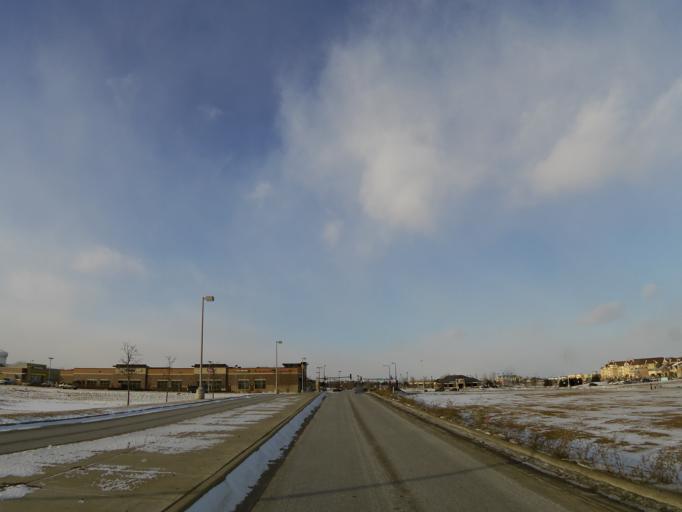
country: US
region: Minnesota
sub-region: Washington County
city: Woodbury
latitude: 44.9394
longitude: -92.9060
